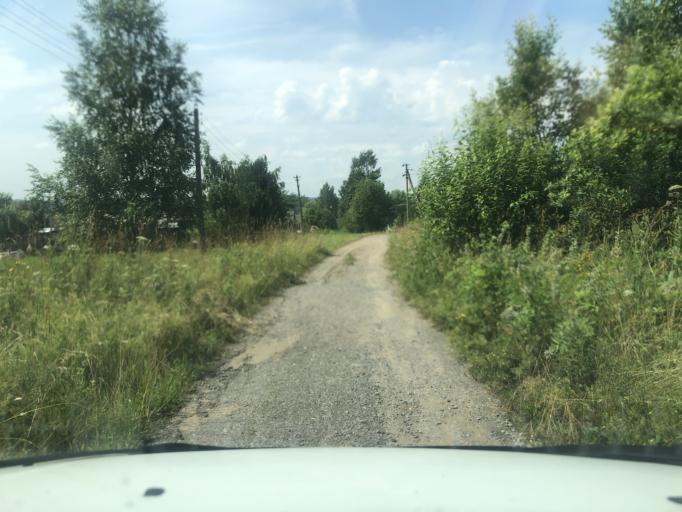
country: RU
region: Jaroslavl
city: Pereslavl'-Zalesskiy
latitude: 57.0457
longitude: 38.8721
